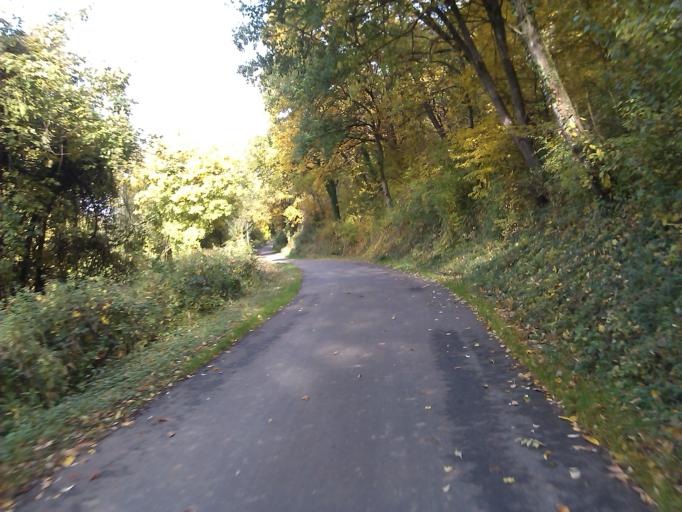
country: DE
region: Rheinland-Pfalz
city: Odenbach
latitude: 49.6789
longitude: 7.6481
